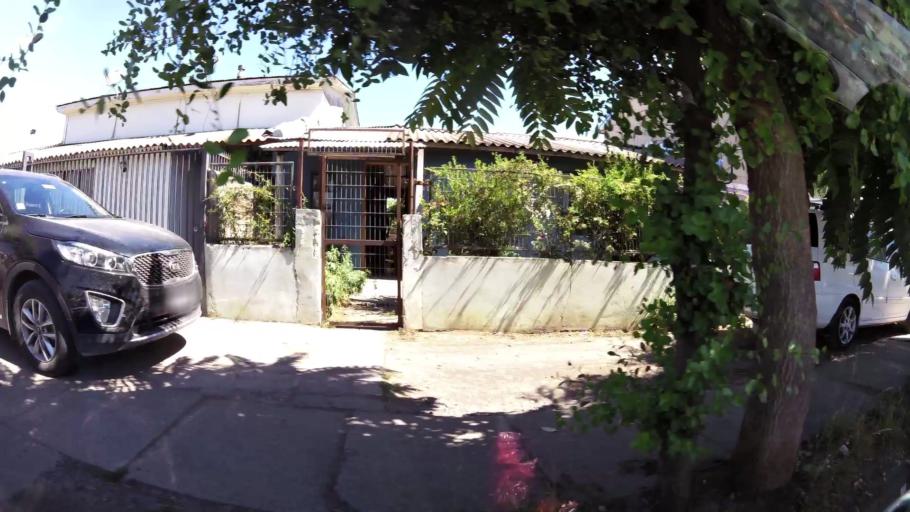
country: CL
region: O'Higgins
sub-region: Provincia de Colchagua
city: Chimbarongo
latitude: -34.5736
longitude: -70.9953
